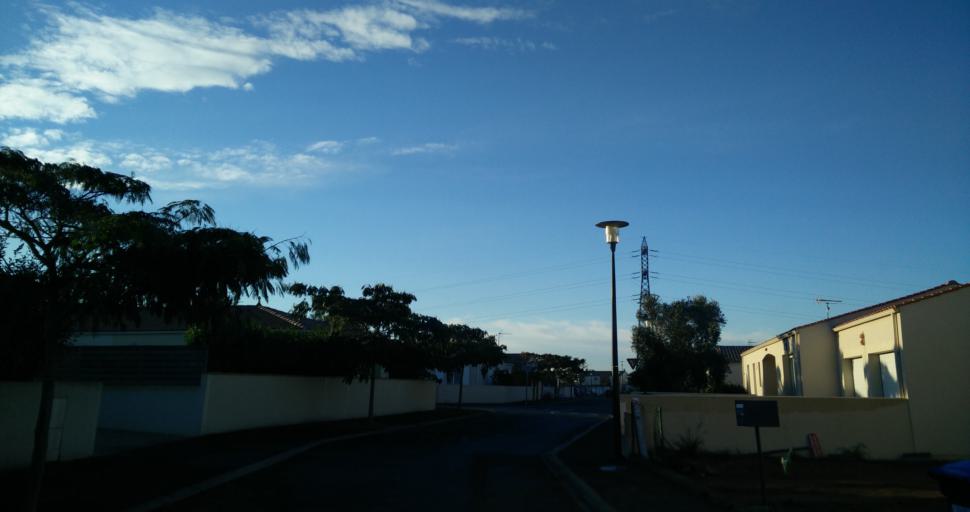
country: FR
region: Poitou-Charentes
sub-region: Departement de la Charente-Maritime
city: Puilboreau
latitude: 46.1840
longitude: -1.1265
